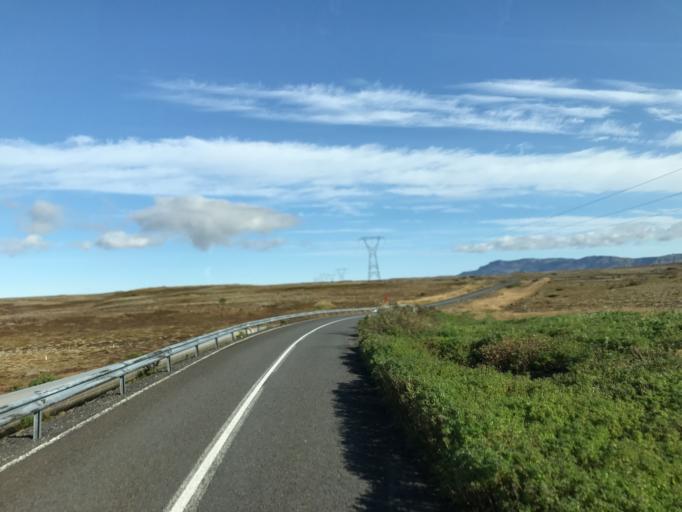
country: IS
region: Capital Region
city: Mosfellsbaer
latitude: 64.1076
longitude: -21.6015
